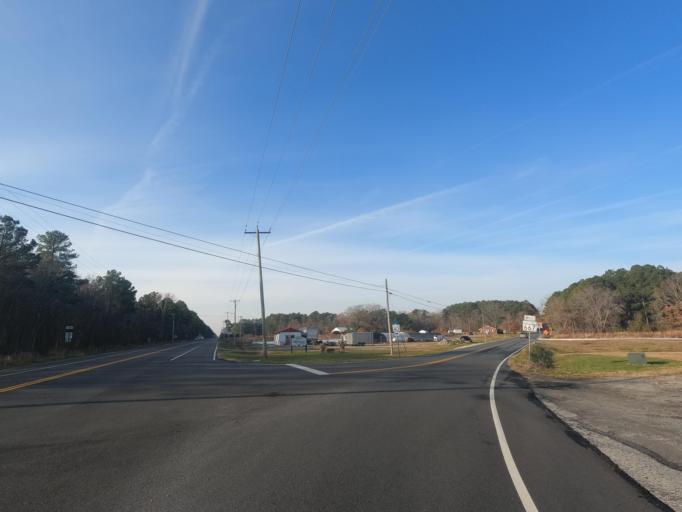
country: US
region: Maryland
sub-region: Somerset County
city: Crisfield
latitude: 38.0332
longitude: -75.7809
